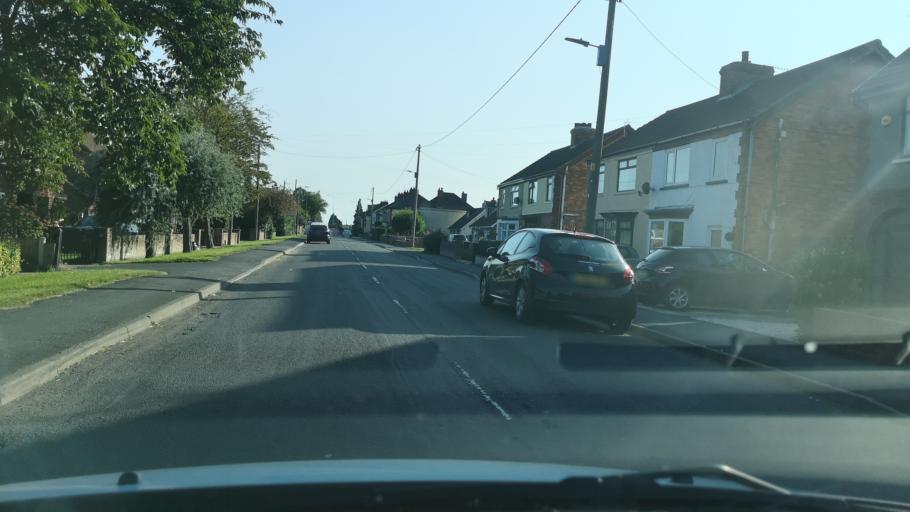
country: GB
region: England
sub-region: North Lincolnshire
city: Gunness
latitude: 53.5923
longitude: -0.7280
